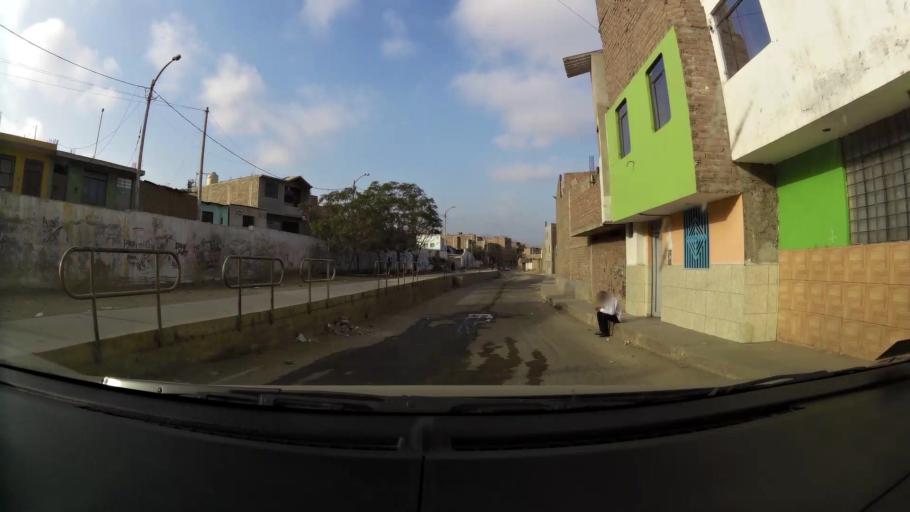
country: PE
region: La Libertad
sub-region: Provincia de Trujillo
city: El Porvenir
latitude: -8.0870
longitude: -79.0174
